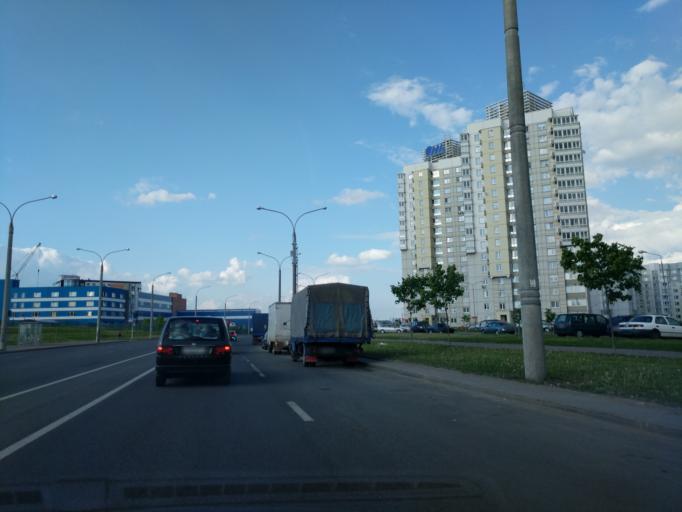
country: BY
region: Minsk
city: Zhdanovichy
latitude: 53.9317
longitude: 27.4265
